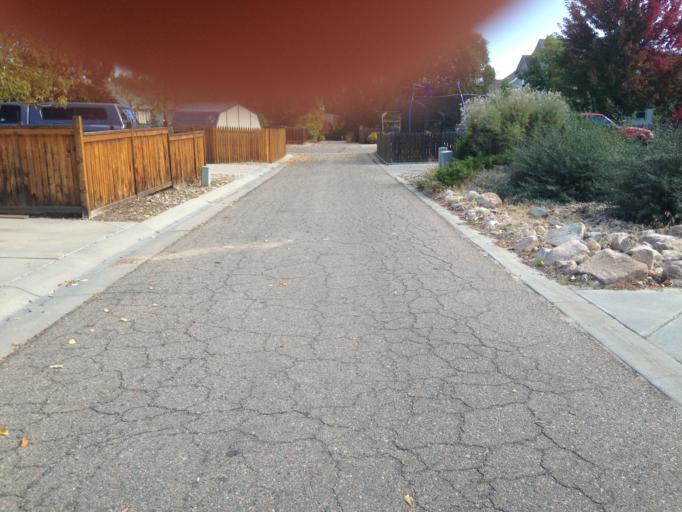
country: US
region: Colorado
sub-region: Larimer County
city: Fort Collins
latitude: 40.5740
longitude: -105.1269
